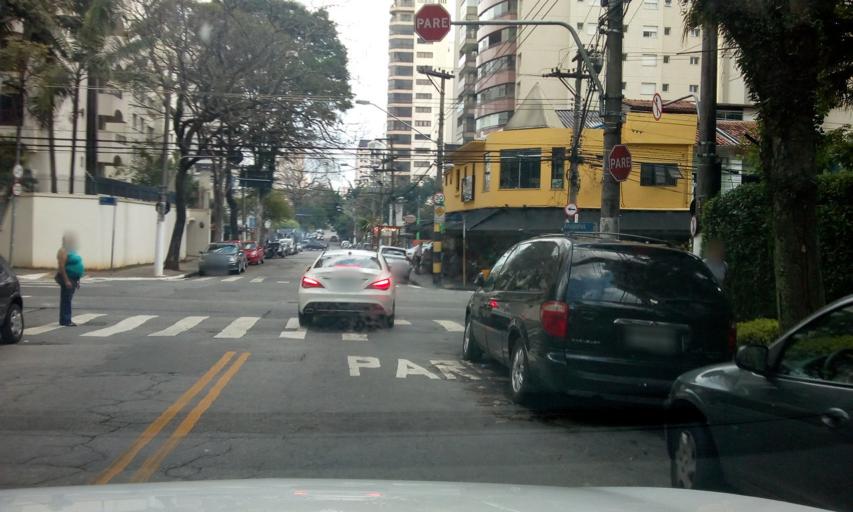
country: BR
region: Sao Paulo
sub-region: Sao Paulo
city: Sao Paulo
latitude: -23.6104
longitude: -46.6612
